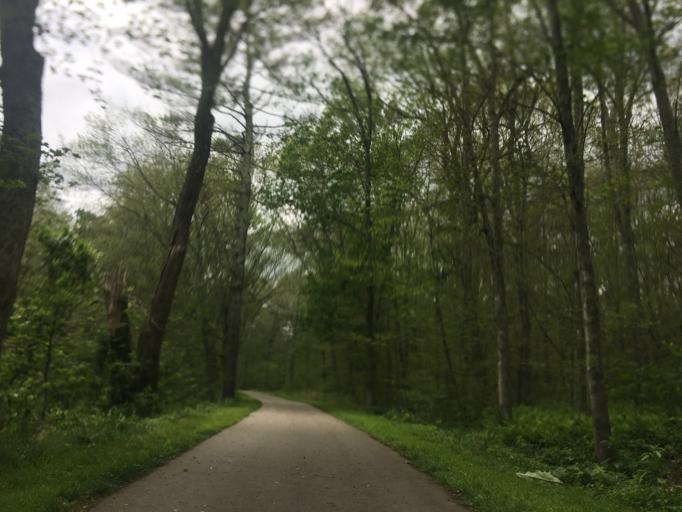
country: US
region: Connecticut
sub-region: Windham County
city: East Brooklyn
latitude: 41.7781
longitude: -71.9035
